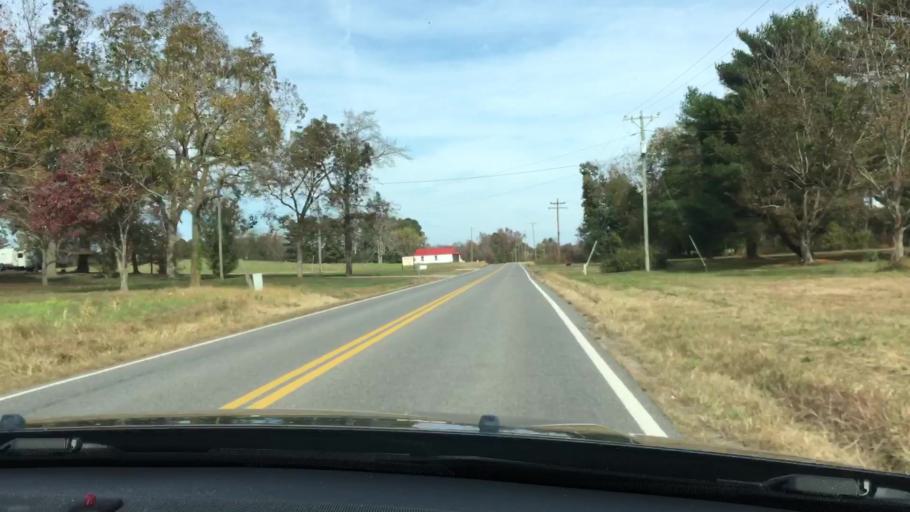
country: US
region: Virginia
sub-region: King William County
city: West Point
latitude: 37.4797
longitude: -76.8185
